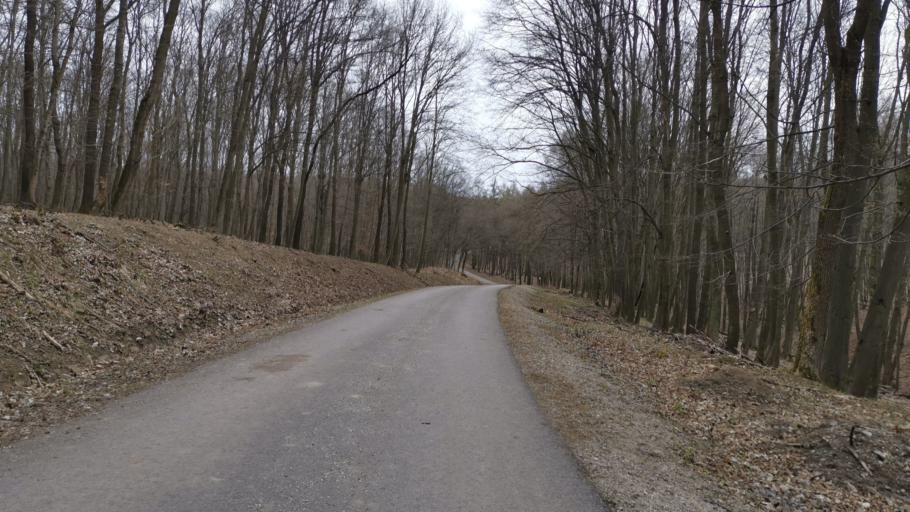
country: CZ
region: South Moravian
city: Petrov
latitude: 48.8112
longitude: 17.3238
